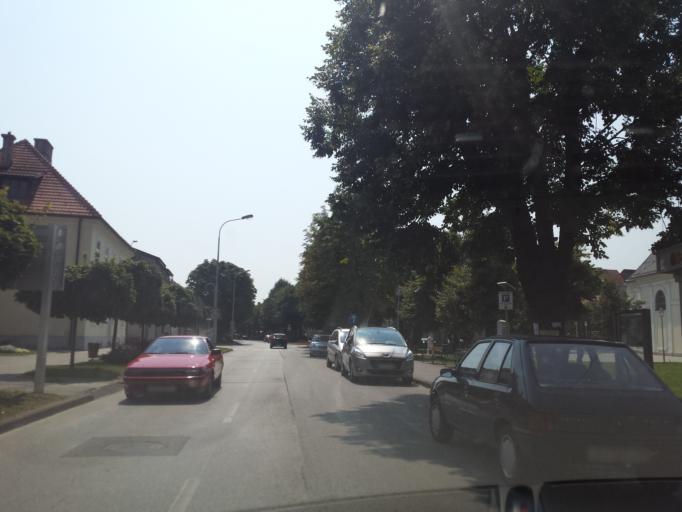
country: HR
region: Karlovacka
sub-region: Grad Ogulin
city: Ogulin
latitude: 45.2665
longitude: 15.2254
